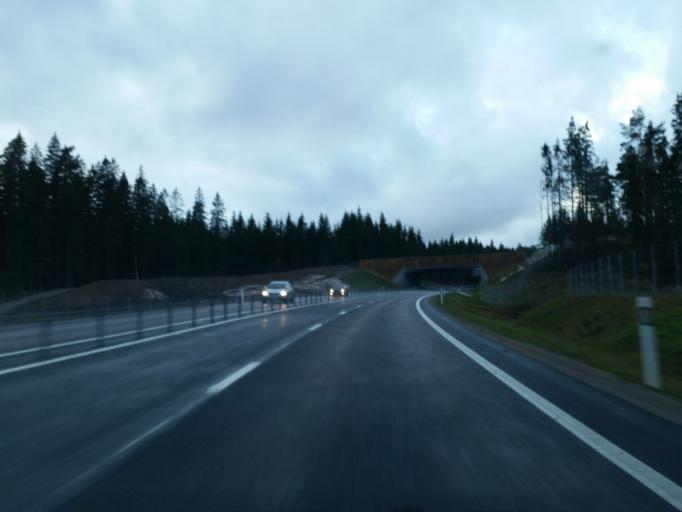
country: SE
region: Vaestra Goetaland
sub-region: Boras Kommun
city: Sjomarken
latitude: 57.7000
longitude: 12.8862
